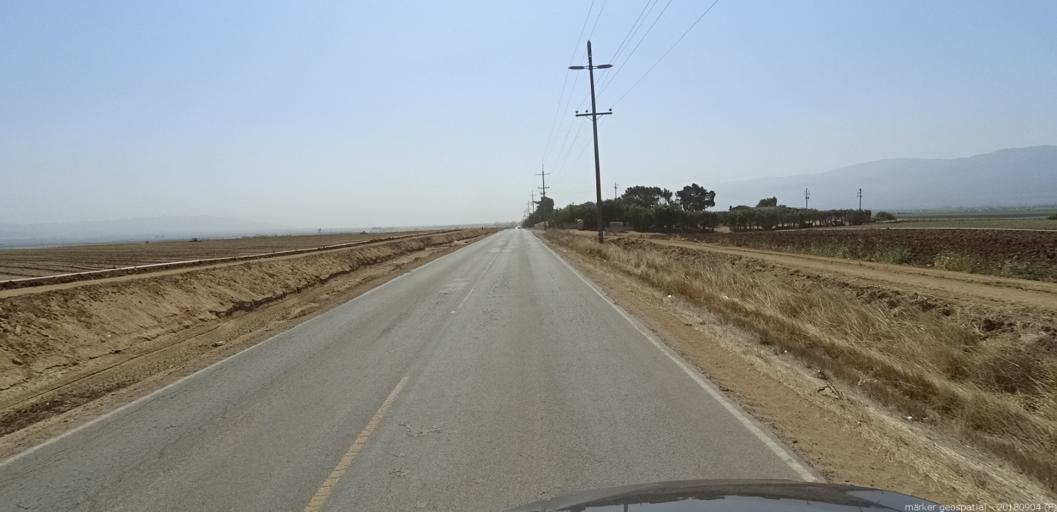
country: US
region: California
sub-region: Monterey County
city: Chualar
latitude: 36.5516
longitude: -121.4742
